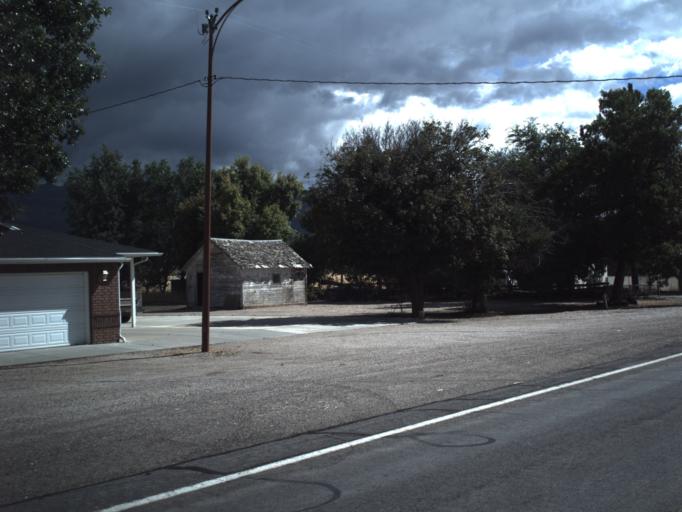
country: US
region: Utah
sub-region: Millard County
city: Fillmore
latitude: 38.8826
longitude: -112.4105
